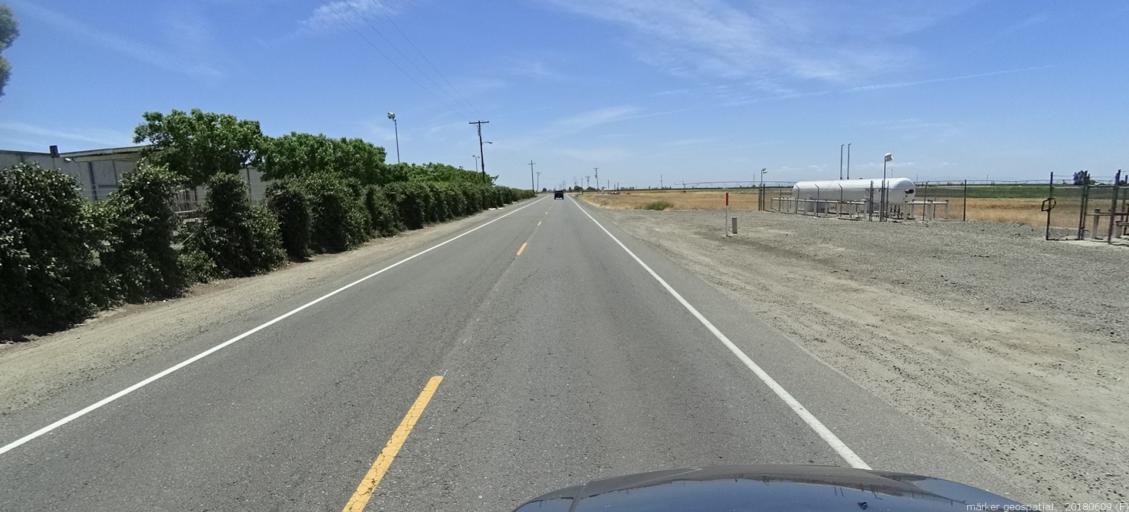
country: US
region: California
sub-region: Madera County
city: Madera
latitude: 36.9294
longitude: -120.1104
